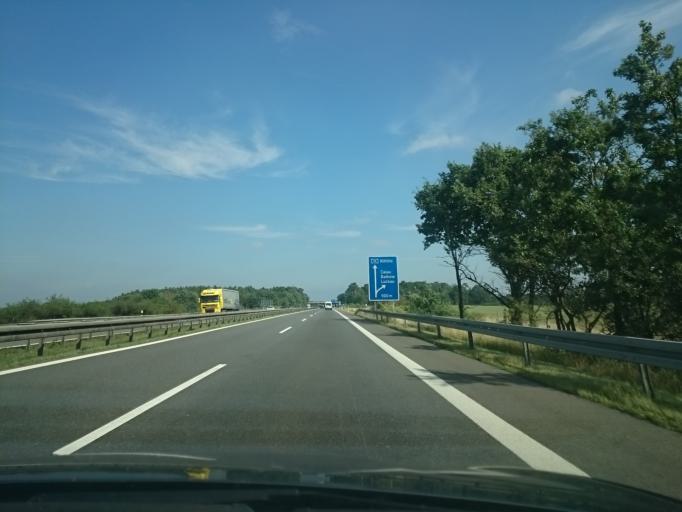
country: DE
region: Brandenburg
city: Calau
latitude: 51.7796
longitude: 13.8730
